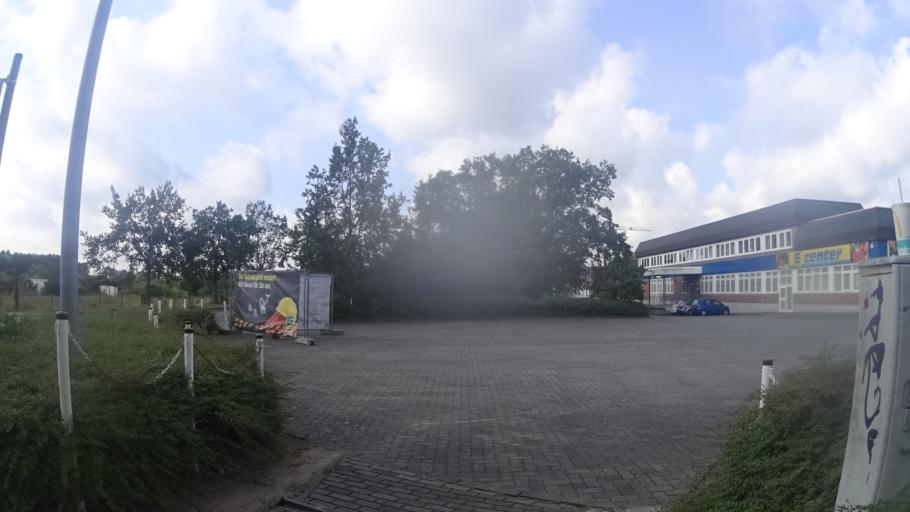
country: DE
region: Brandenburg
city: Wittenberge
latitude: 53.0033
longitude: 11.7233
